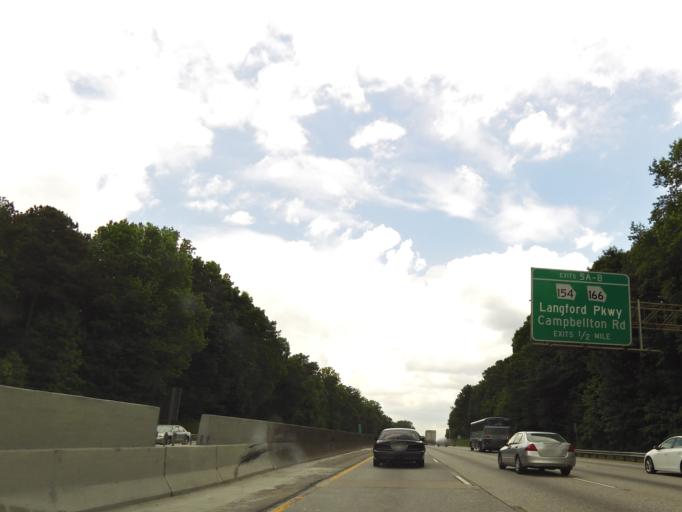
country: US
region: Georgia
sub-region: Fulton County
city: College Park
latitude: 33.6789
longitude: -84.4995
